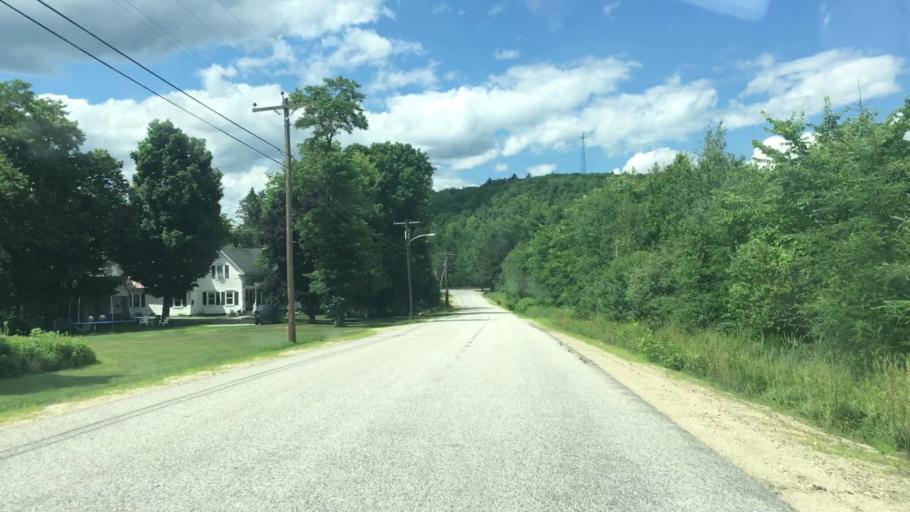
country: US
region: Maine
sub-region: Franklin County
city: Jay
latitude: 44.5328
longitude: -70.2260
